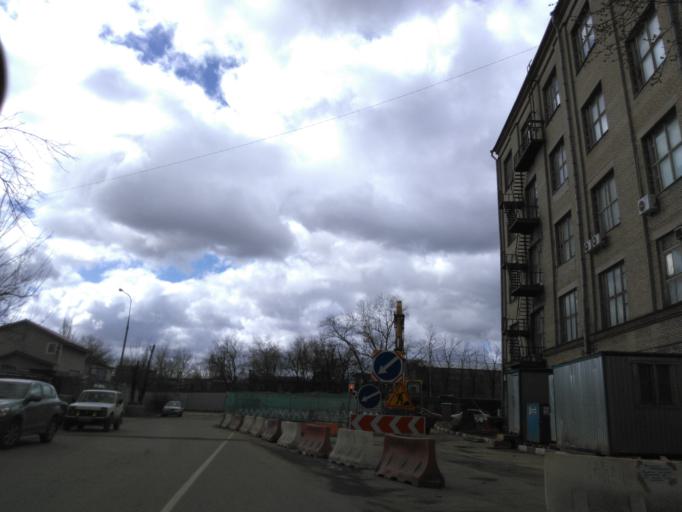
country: RU
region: Moskovskaya
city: Koptevo
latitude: 55.8310
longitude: 37.5119
